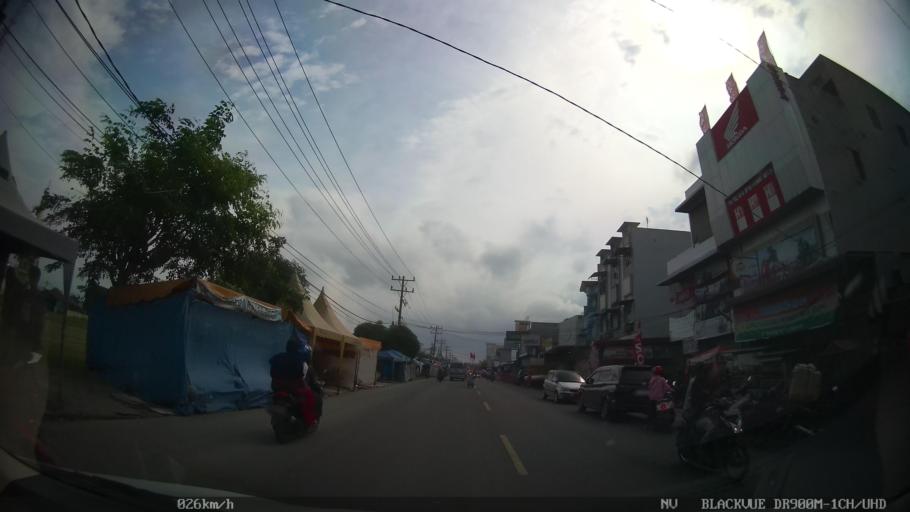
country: ID
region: North Sumatra
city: Medan
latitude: 3.6005
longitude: 98.7572
